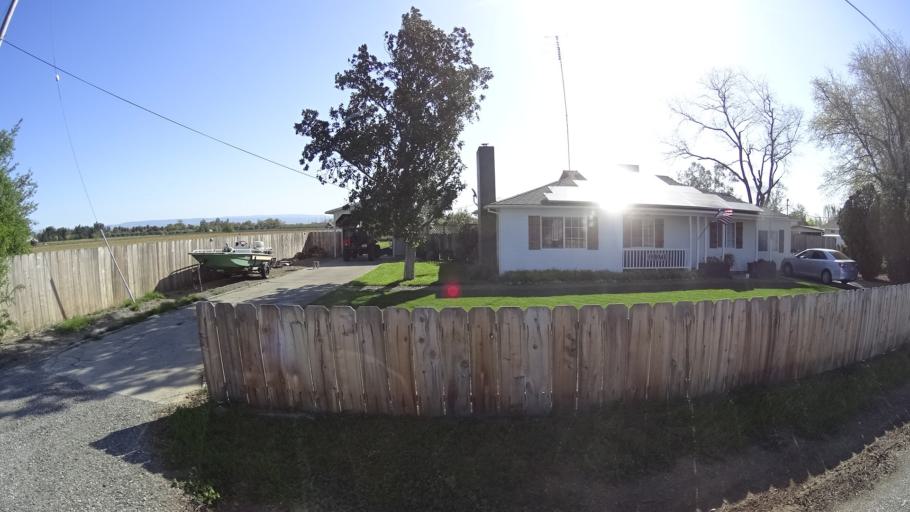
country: US
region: California
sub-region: Glenn County
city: Hamilton City
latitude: 39.7932
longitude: -122.0665
